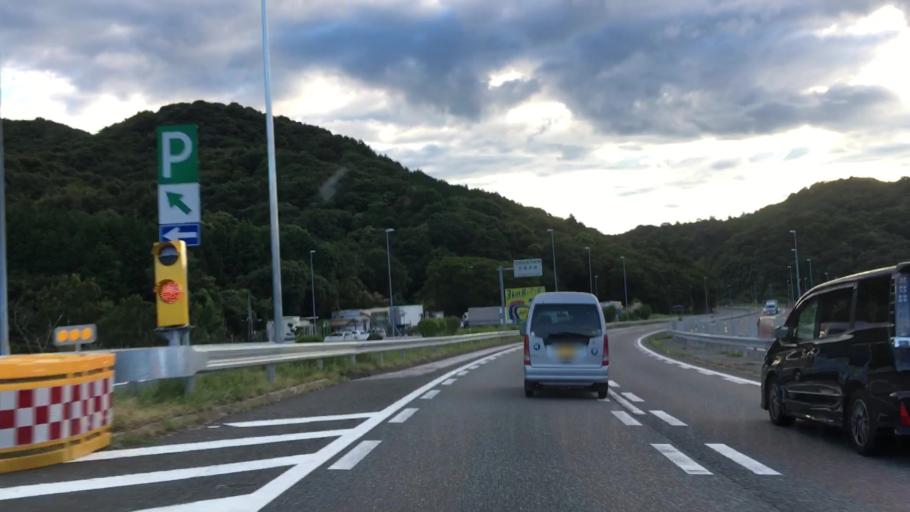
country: JP
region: Yamaguchi
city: Onoda
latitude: 34.1196
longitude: 131.2085
